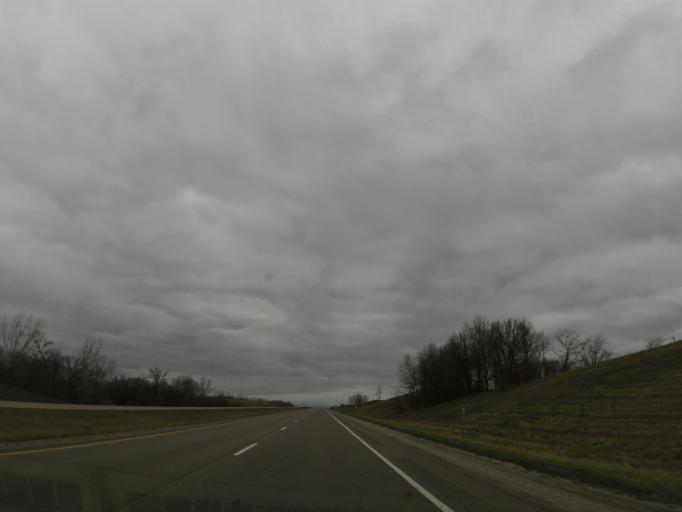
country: US
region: Iowa
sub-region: Washington County
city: Washington
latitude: 41.3811
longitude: -91.5510
